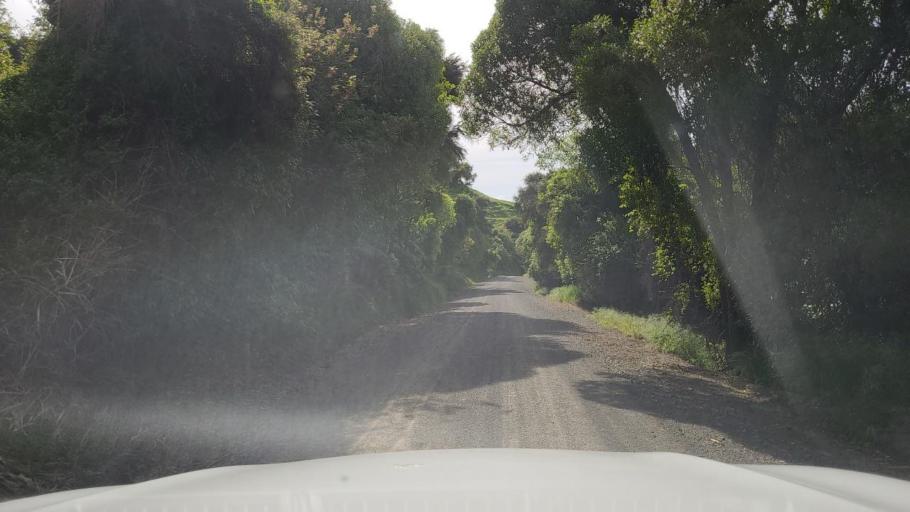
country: NZ
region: Hawke's Bay
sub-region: Napier City
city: Taradale
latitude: -39.3475
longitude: 176.6725
